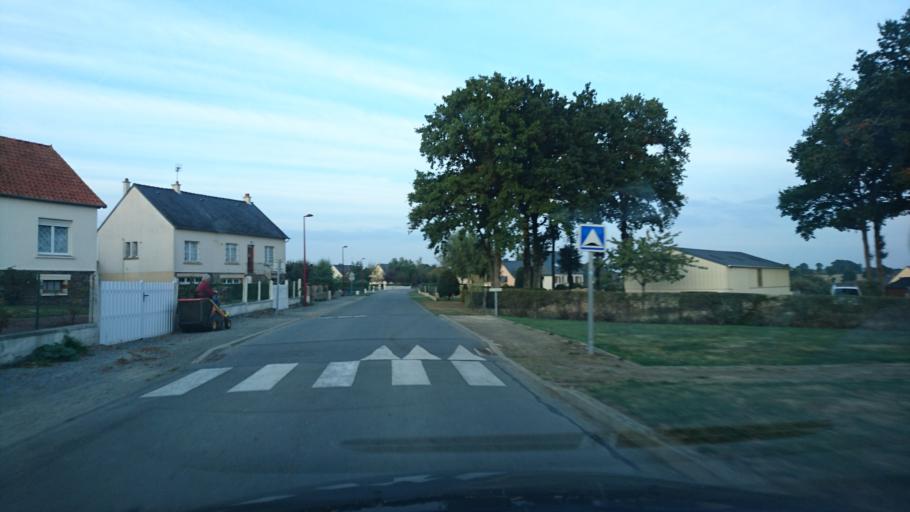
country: FR
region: Brittany
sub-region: Departement du Morbihan
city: Guer
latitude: 47.8775
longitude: -2.0792
